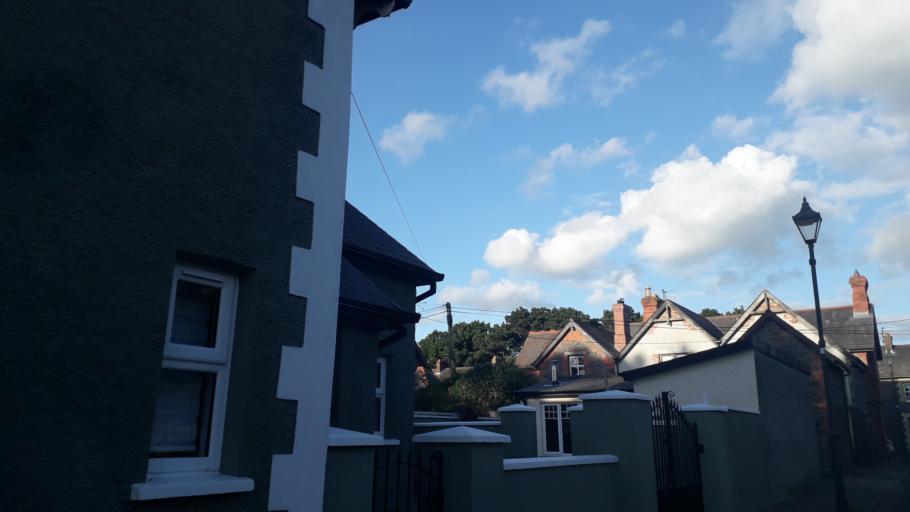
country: IE
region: Leinster
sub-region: Lu
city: Carlingford
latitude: 54.0315
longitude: -6.1336
